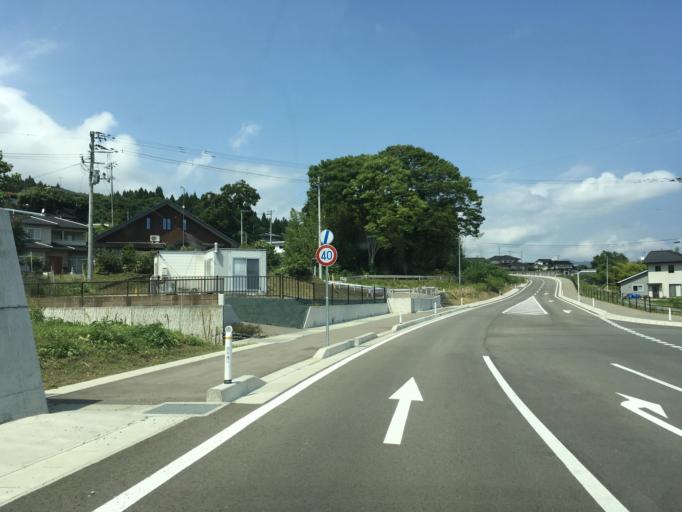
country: JP
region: Iwate
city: Ofunato
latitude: 39.0077
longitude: 141.7102
